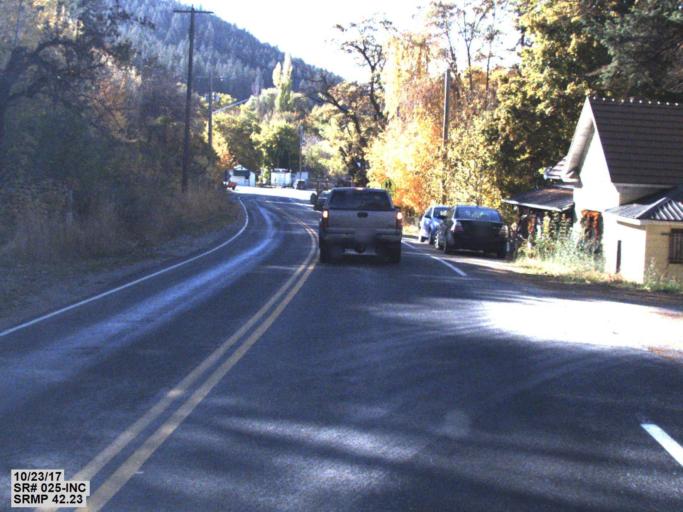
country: US
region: Washington
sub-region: Lincoln County
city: Davenport
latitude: 48.1176
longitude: -118.2001
